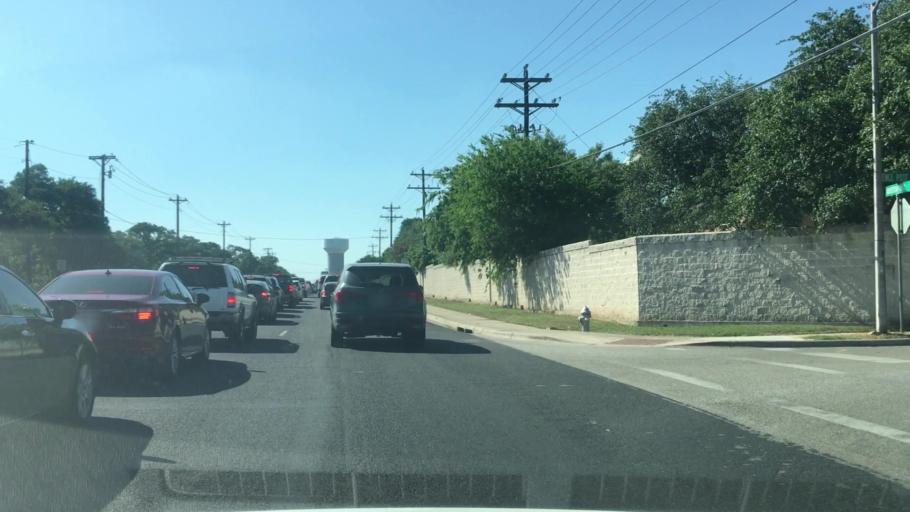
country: US
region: Texas
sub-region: Williamson County
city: Anderson Mill
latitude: 30.4524
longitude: -97.8219
